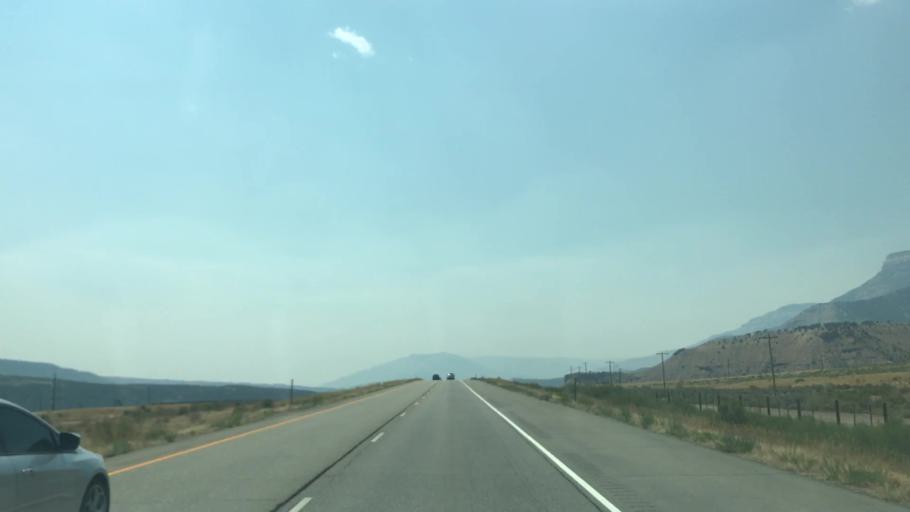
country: US
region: Colorado
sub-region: Garfield County
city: Rifle
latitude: 39.5028
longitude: -107.9047
